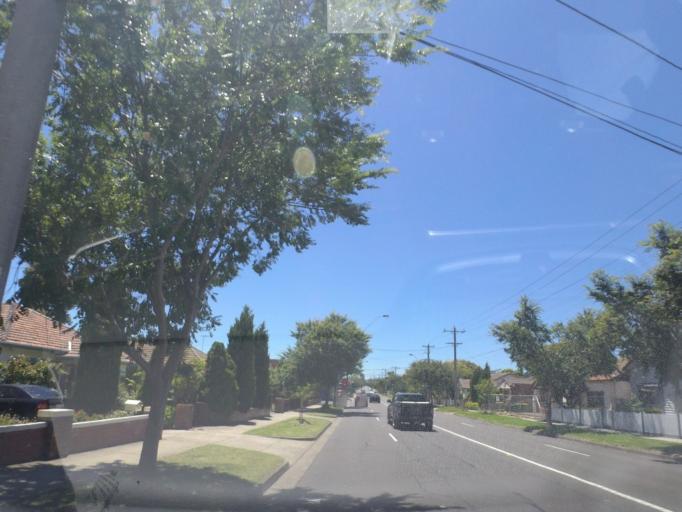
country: AU
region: Victoria
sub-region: Darebin
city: Reservoir
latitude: -37.7289
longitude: 145.0007
